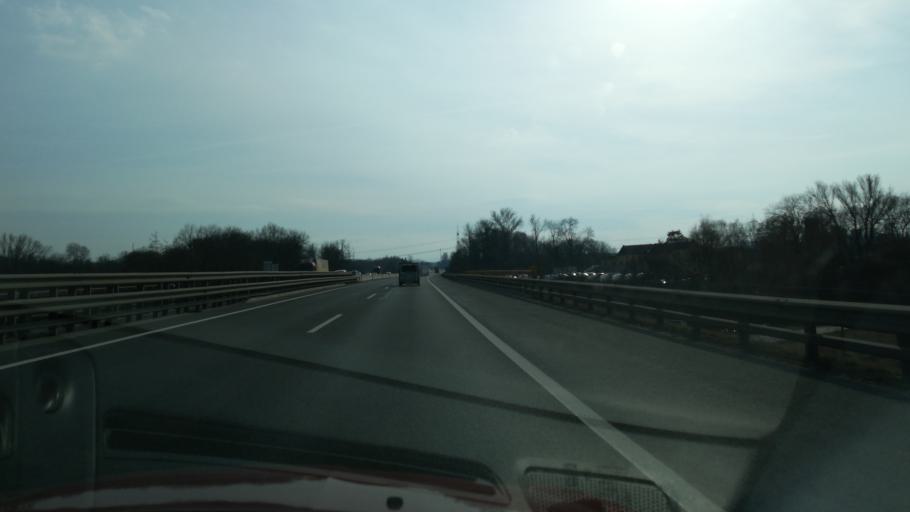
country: AT
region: Lower Austria
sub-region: Politischer Bezirk Sankt Polten
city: Traismauer
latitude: 48.3347
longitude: 15.7224
